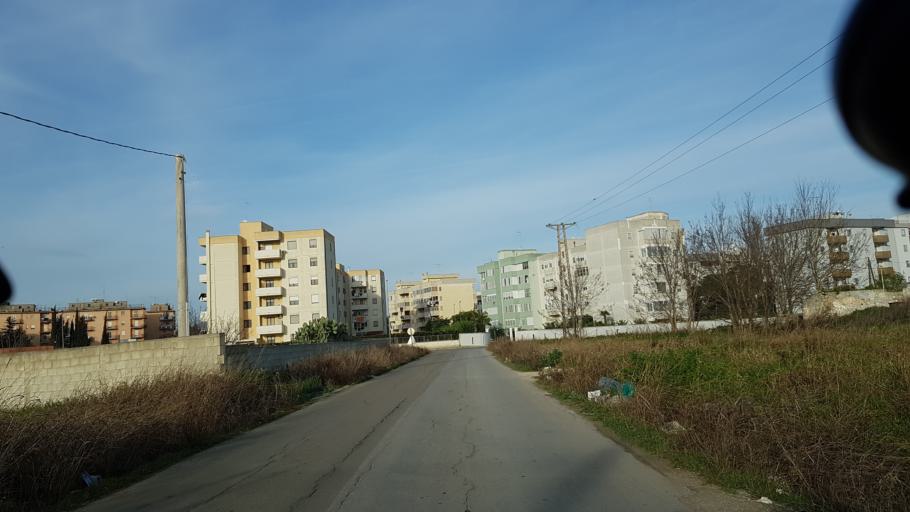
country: IT
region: Apulia
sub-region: Provincia di Brindisi
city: Brindisi
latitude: 40.6162
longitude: 17.9174
